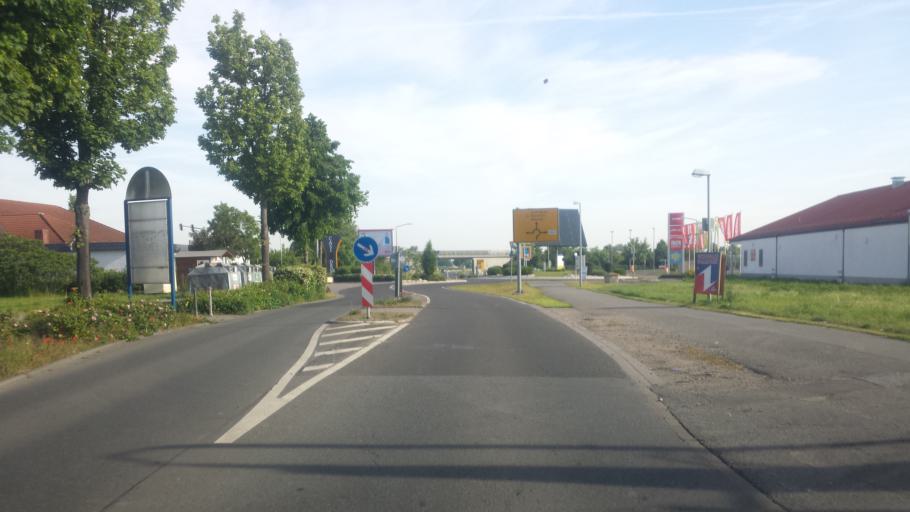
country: DE
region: Hesse
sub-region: Regierungsbezirk Darmstadt
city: Burstadt
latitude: 49.6523
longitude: 8.4520
